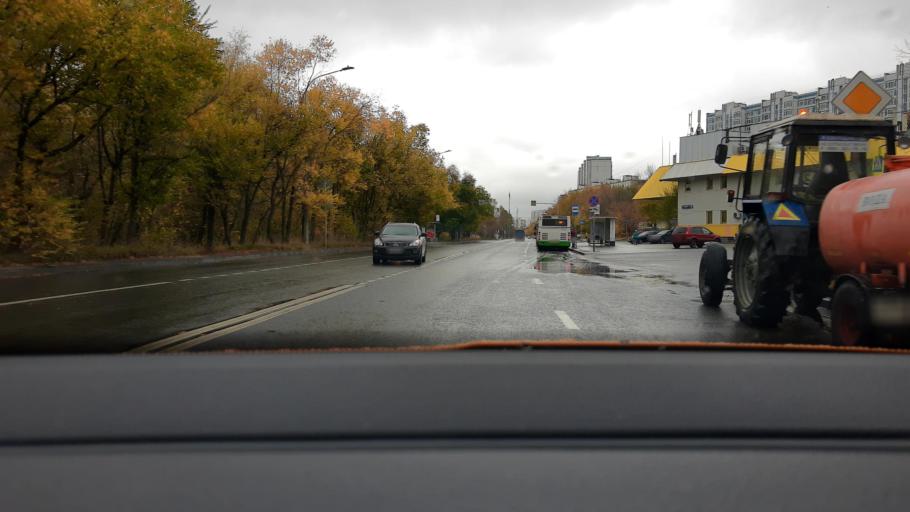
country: RU
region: Moscow
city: Strogino
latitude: 55.8180
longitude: 37.4030
